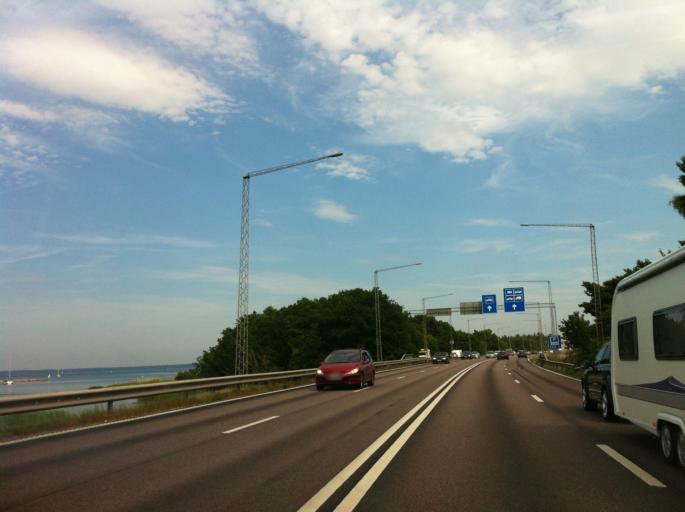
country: SE
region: Kalmar
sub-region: Kalmar Kommun
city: Kalmar
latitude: 56.6849
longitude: 16.3619
